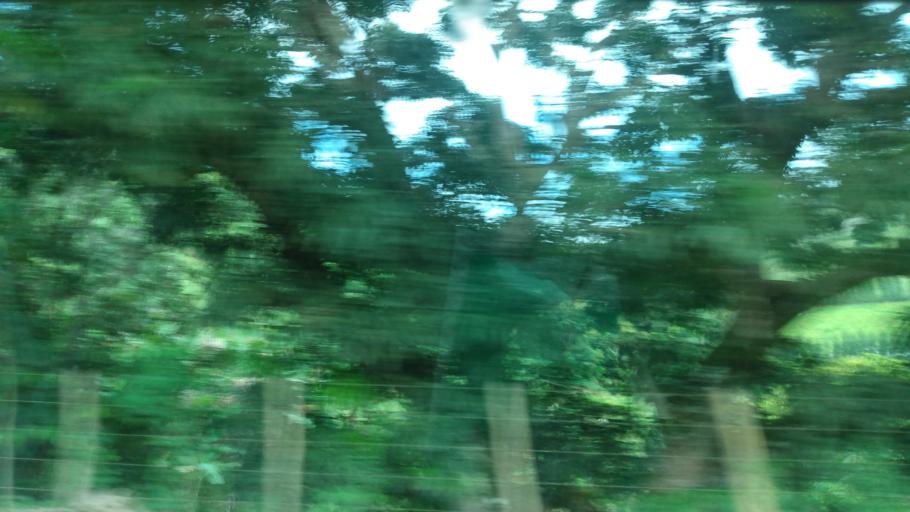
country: BR
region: Pernambuco
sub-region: Maraial
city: Maraial
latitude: -8.7211
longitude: -35.7824
